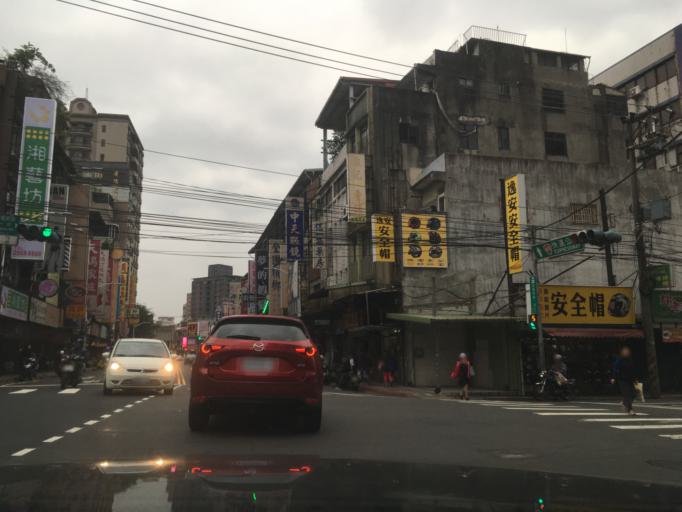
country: TW
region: Taipei
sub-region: Taipei
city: Banqiao
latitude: 25.0077
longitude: 121.4566
